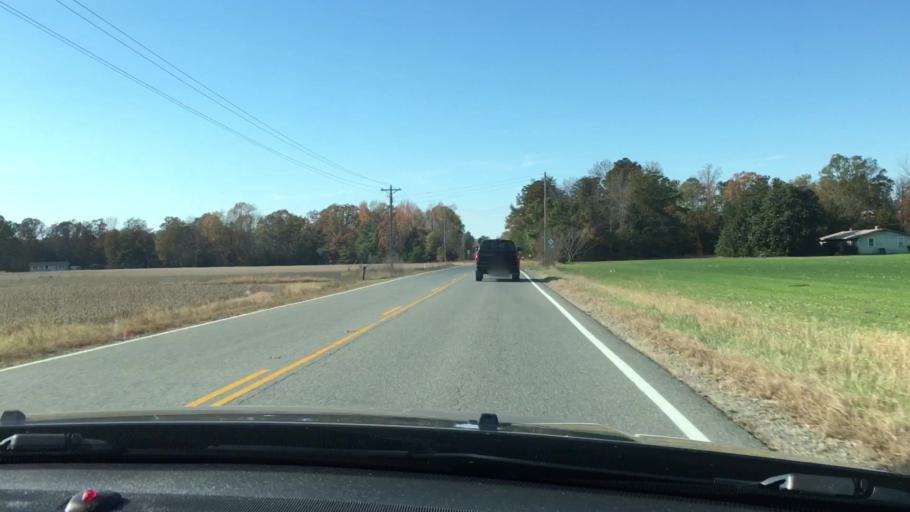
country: US
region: Virginia
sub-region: Hanover County
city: Hanover
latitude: 37.8282
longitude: -77.3470
